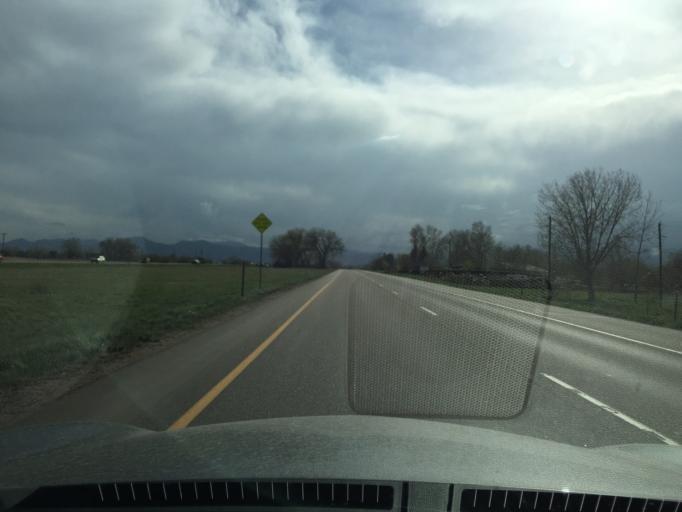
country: US
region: Colorado
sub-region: Boulder County
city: Niwot
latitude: 40.1194
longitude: -105.1558
